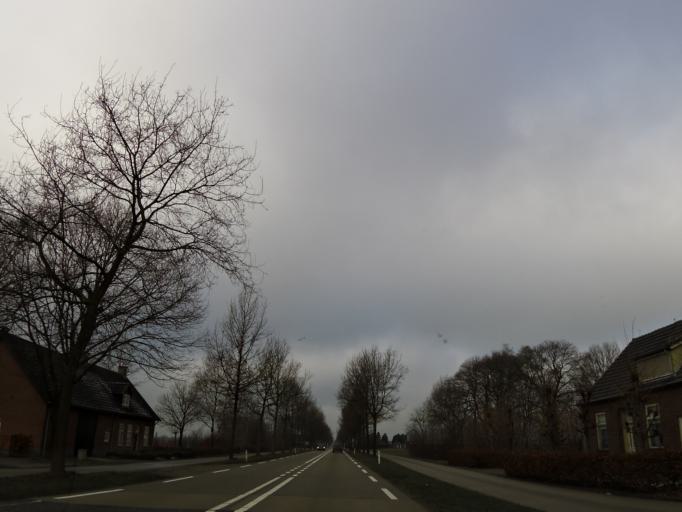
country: NL
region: North Brabant
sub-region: Gemeente Sint Anthonis
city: Sint Anthonis
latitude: 51.5391
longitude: 5.8419
